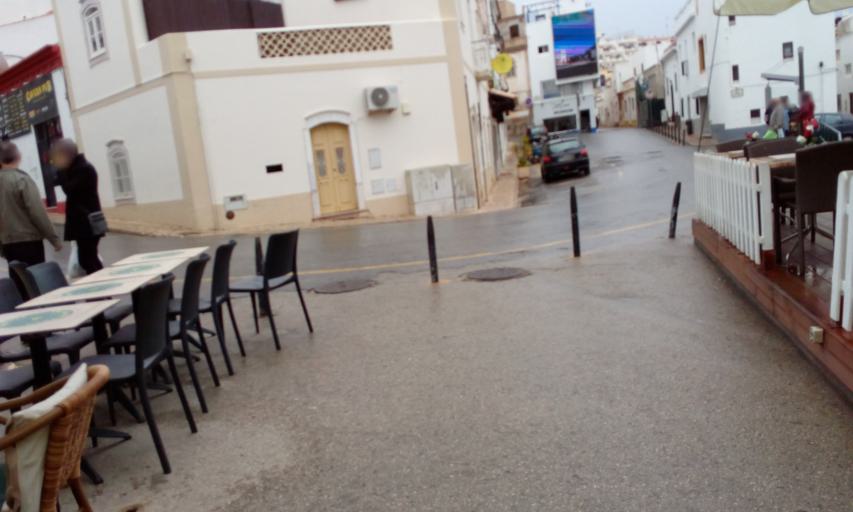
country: PT
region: Faro
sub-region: Albufeira
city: Albufeira
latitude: 37.0889
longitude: -8.2510
